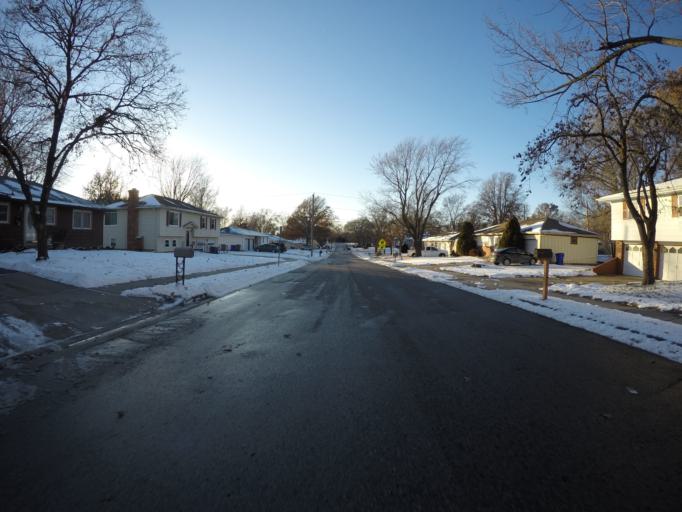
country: US
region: Kansas
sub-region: Johnson County
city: Olathe
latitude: 38.8913
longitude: -94.8319
